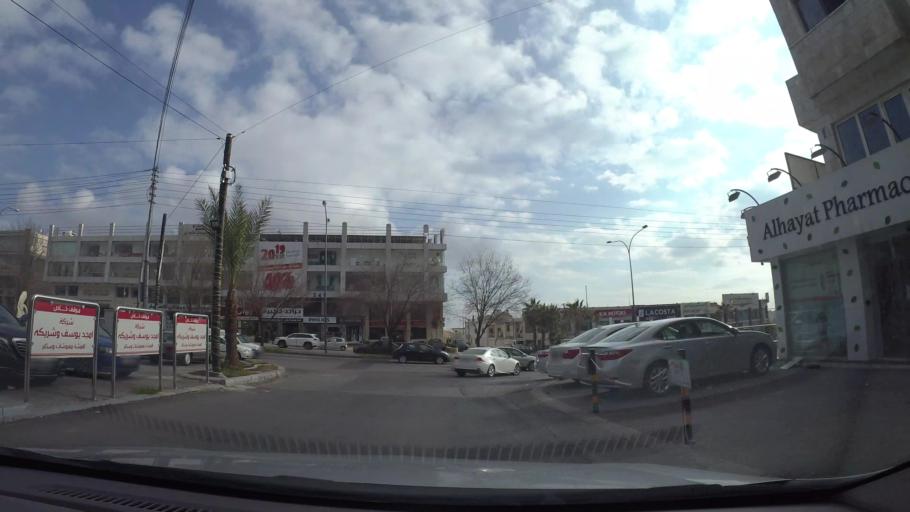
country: JO
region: Amman
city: Wadi as Sir
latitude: 31.9754
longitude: 35.8446
